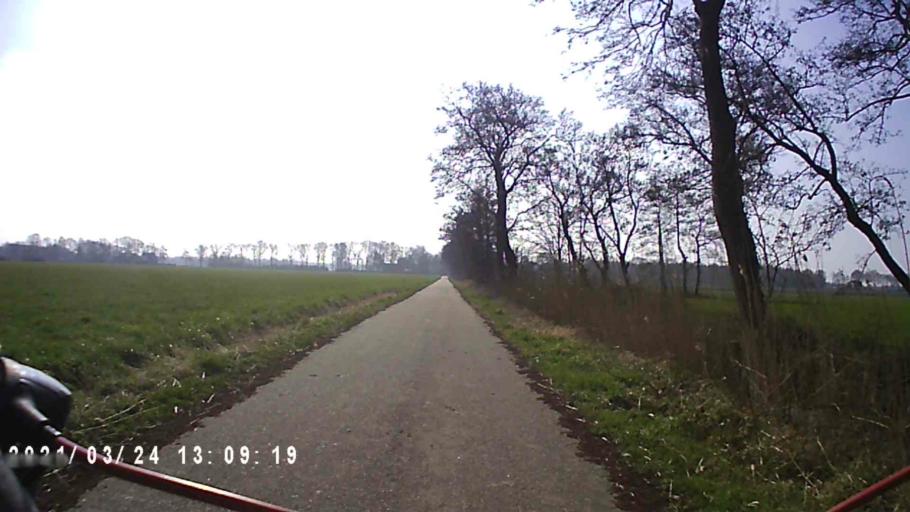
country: NL
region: Groningen
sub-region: Gemeente Leek
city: Leek
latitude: 53.1241
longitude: 6.3047
